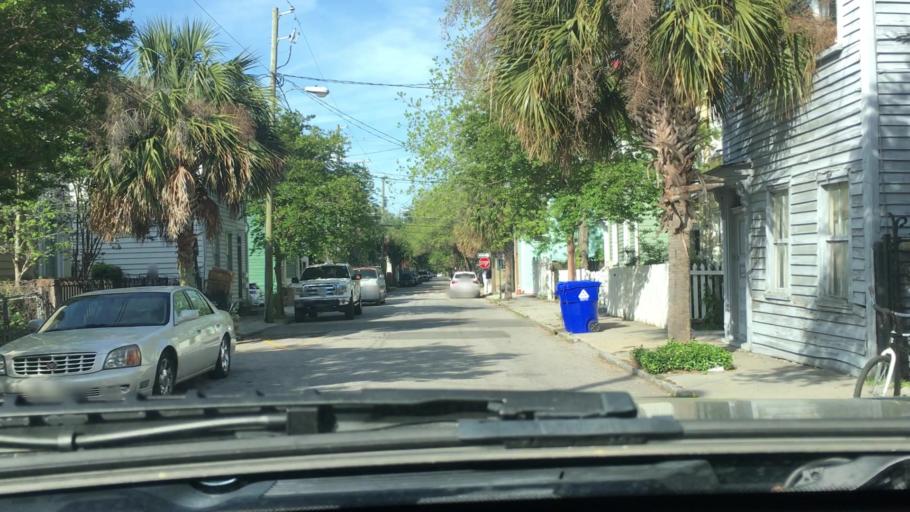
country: US
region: South Carolina
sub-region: Charleston County
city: Charleston
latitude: 32.7934
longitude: -79.9436
